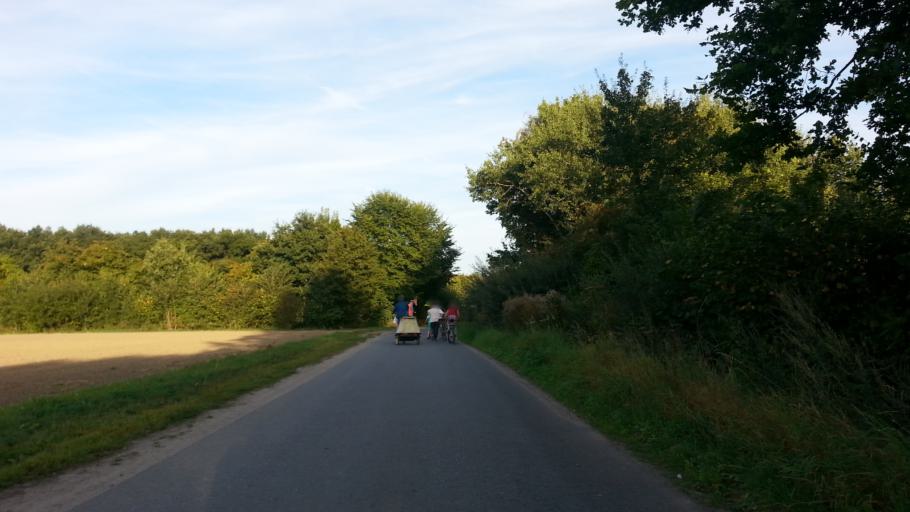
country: DE
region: North Rhine-Westphalia
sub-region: Regierungsbezirk Munster
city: Muenster
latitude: 51.9417
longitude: 7.5853
